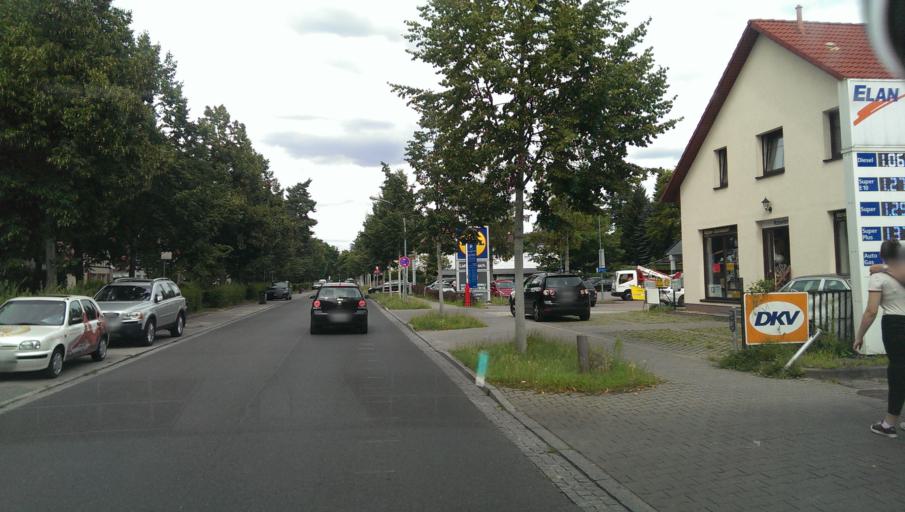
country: DE
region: Brandenburg
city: Kleinmachnow
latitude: 52.4150
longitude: 13.2239
